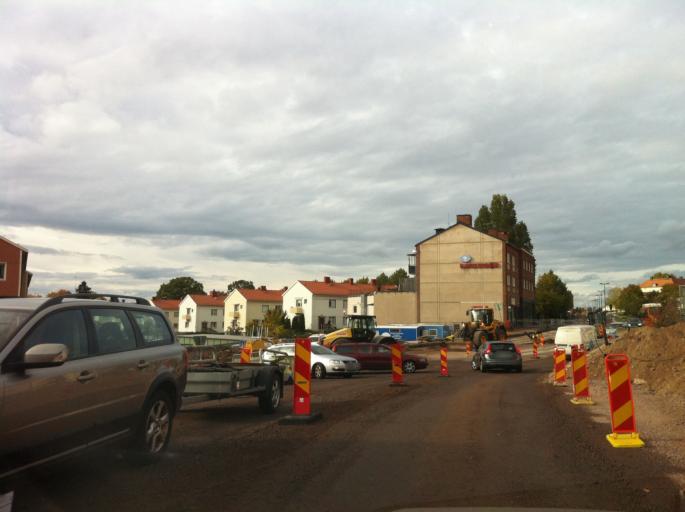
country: SE
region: OEstergoetland
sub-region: Motala Kommun
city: Motala
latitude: 58.5377
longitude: 15.0360
